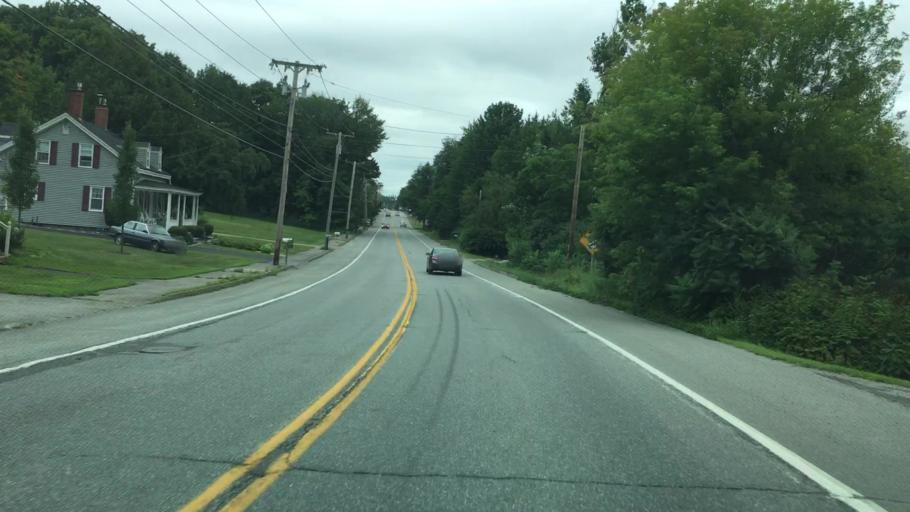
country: US
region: Maine
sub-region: Penobscot County
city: Orrington
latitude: 44.7282
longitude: -68.8422
